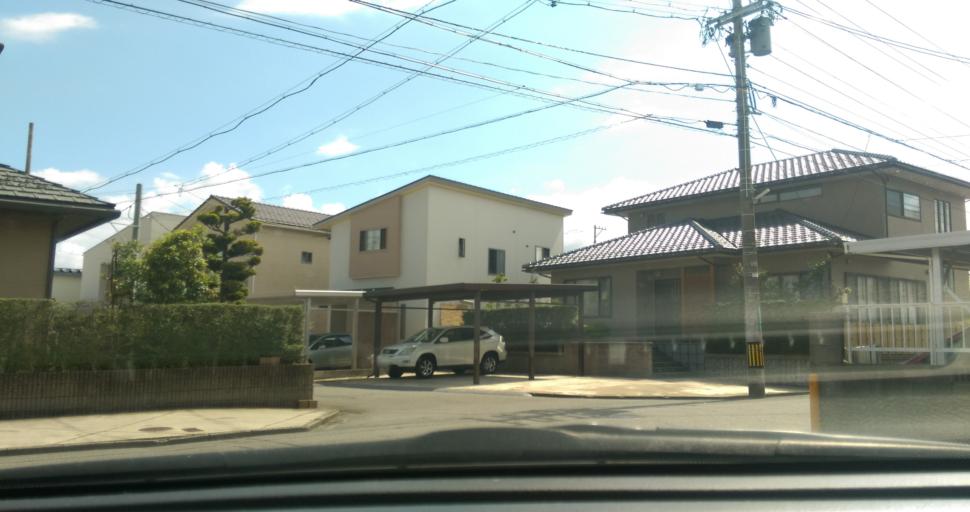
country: JP
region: Fukui
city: Fukui-shi
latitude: 36.0759
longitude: 136.2019
